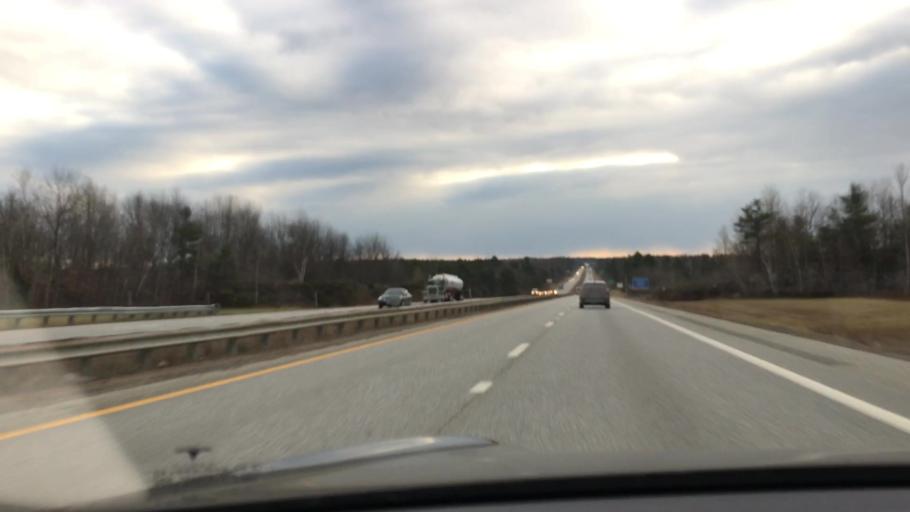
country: US
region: Maine
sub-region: Kennebec County
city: Hallowell
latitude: 44.2636
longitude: -69.8069
